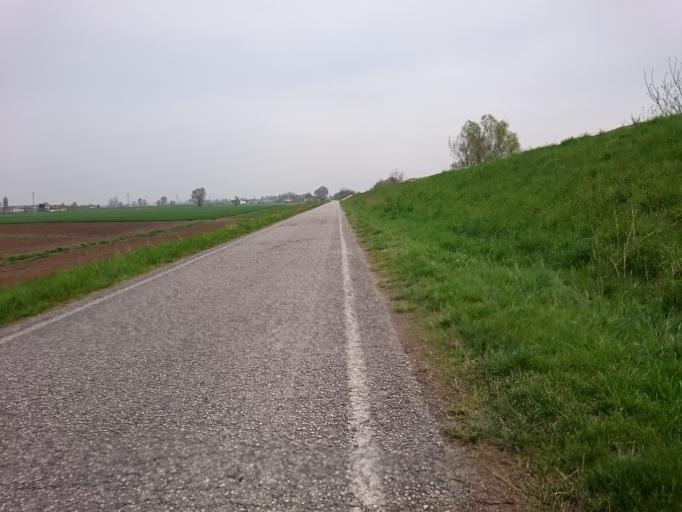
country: IT
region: Veneto
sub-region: Provincia di Rovigo
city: San Martino di Venezze
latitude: 45.1482
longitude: 11.8502
